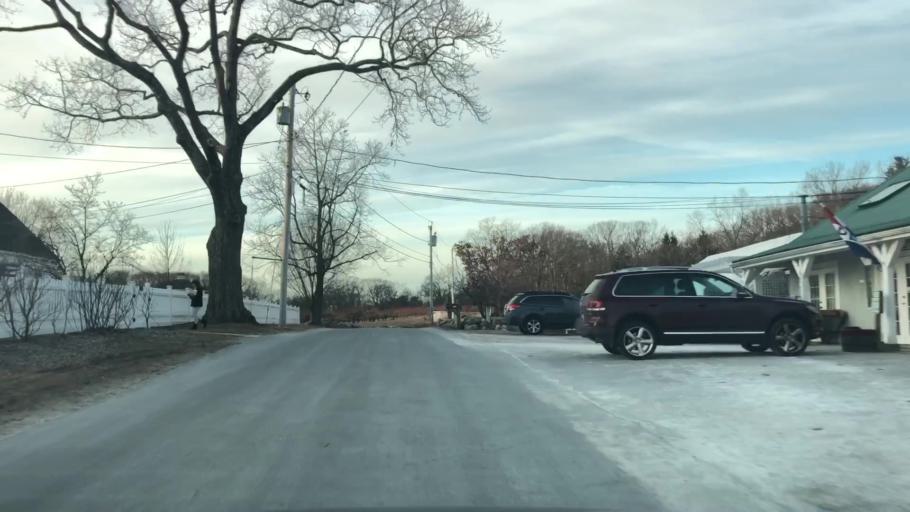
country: US
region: Massachusetts
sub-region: Essex County
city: North Andover
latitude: 42.6901
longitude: -71.0748
